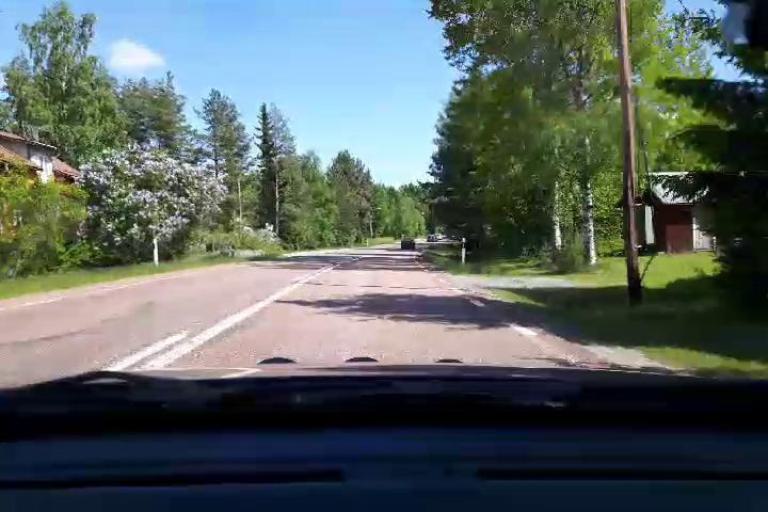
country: SE
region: Gaevleborg
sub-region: Hudiksvalls Kommun
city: Delsbo
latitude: 61.8012
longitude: 16.4890
